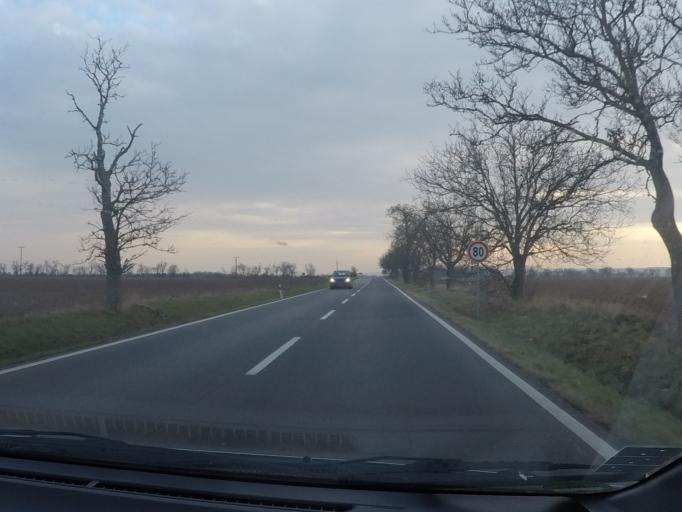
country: SK
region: Nitriansky
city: Zeliezovce
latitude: 48.0732
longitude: 18.5274
